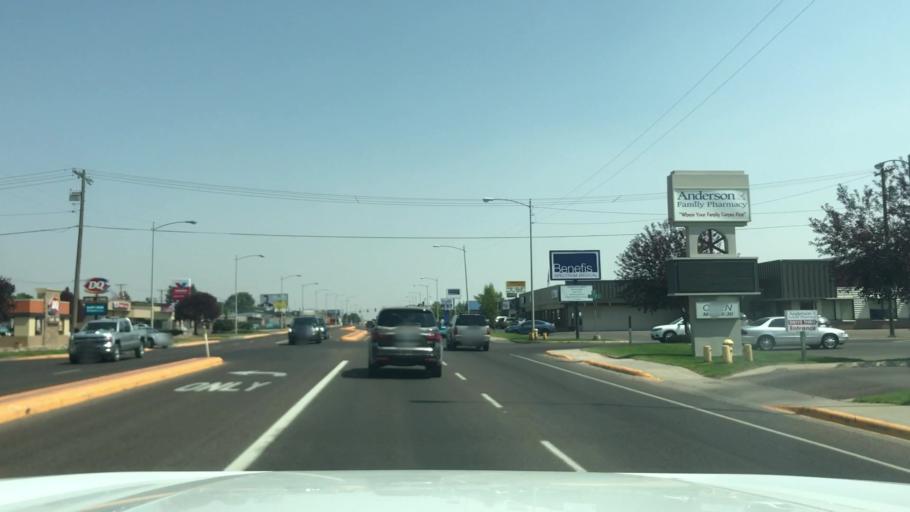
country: US
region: Montana
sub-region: Cascade County
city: Great Falls
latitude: 47.4940
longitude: -111.2580
